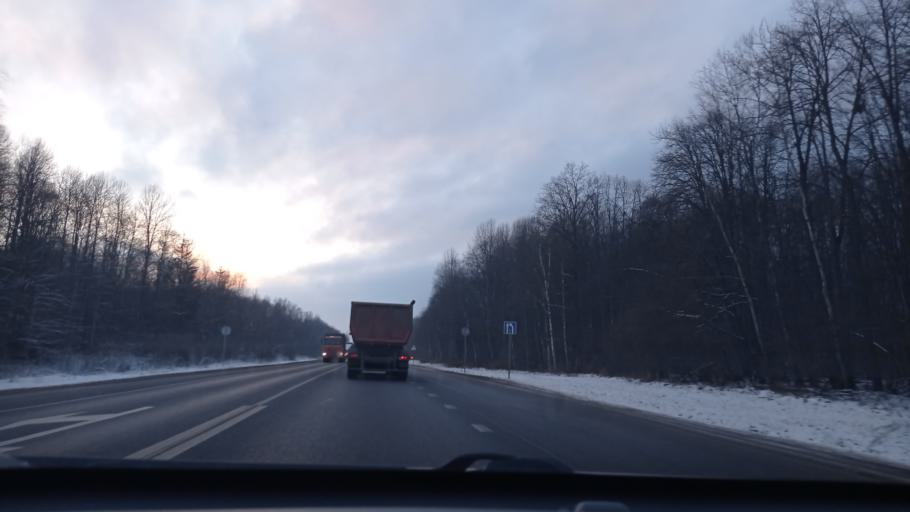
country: RU
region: Moskovskaya
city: Ateptsevo
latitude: 55.1752
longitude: 36.8779
